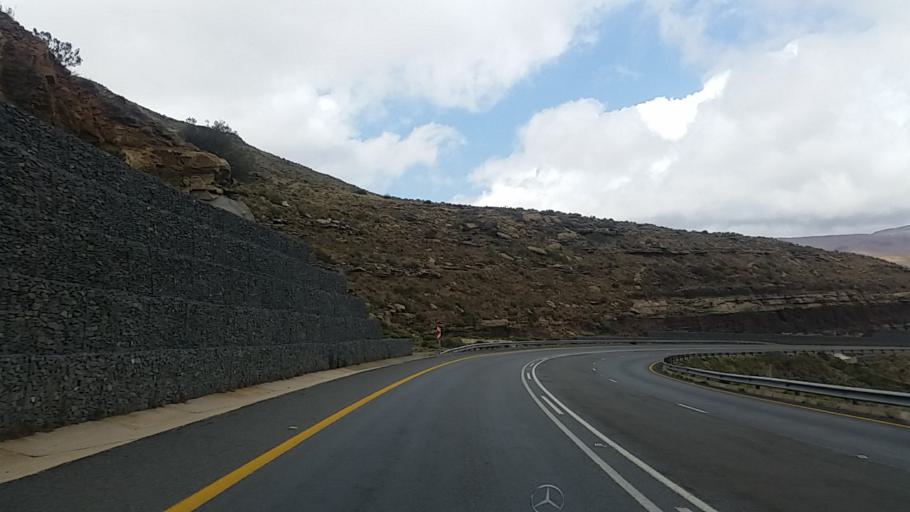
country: ZA
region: Eastern Cape
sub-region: Chris Hani District Municipality
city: Middelburg
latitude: -31.8417
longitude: 24.8691
